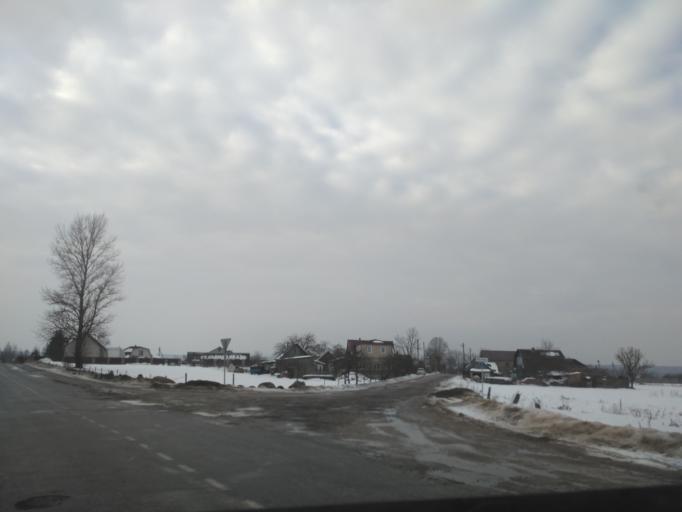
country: BY
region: Minsk
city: Zamostochcha
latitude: 53.8911
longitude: 27.9229
